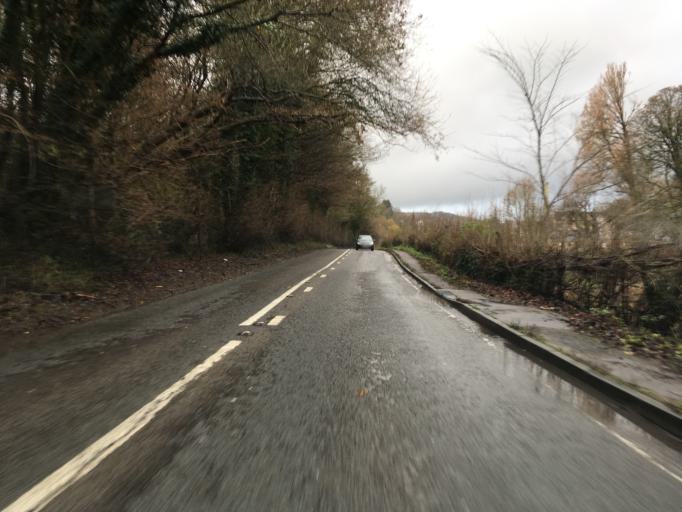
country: GB
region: England
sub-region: Gloucestershire
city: Nailsworth
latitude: 51.7011
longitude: -2.2250
